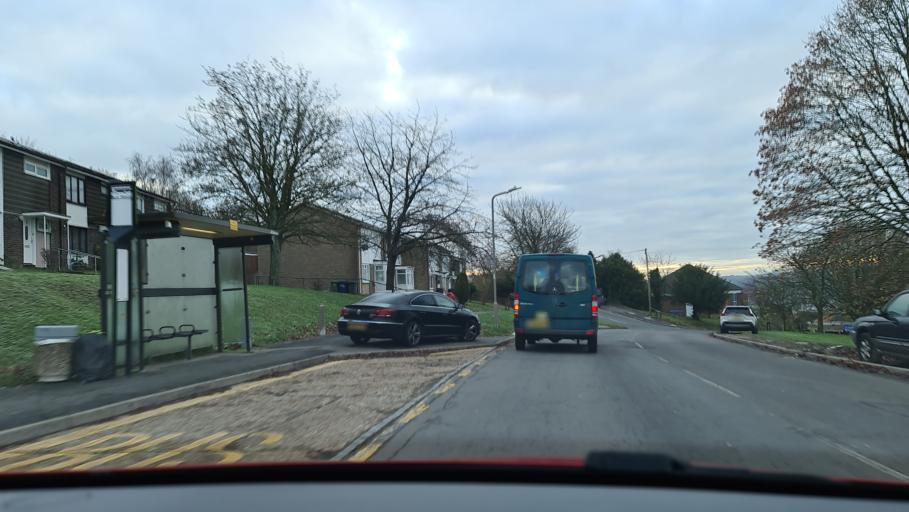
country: GB
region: England
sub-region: Buckinghamshire
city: High Wycombe
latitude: 51.6388
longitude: -0.7652
